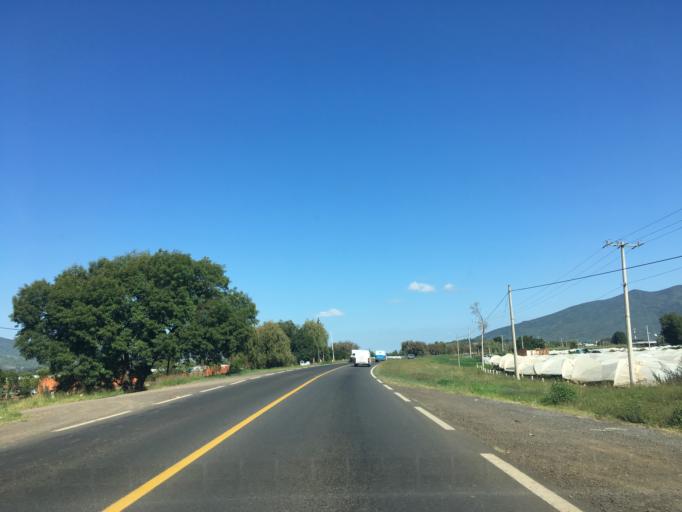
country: MX
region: Mexico
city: Tangancicuaro de Arista
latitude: 19.8725
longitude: -102.1967
